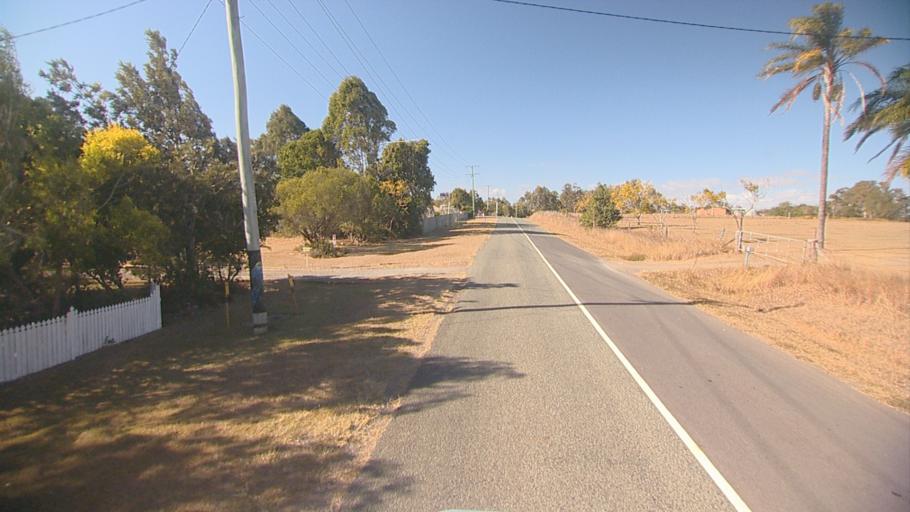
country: AU
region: Queensland
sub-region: Logan
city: Cedar Vale
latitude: -27.8556
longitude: 152.9720
